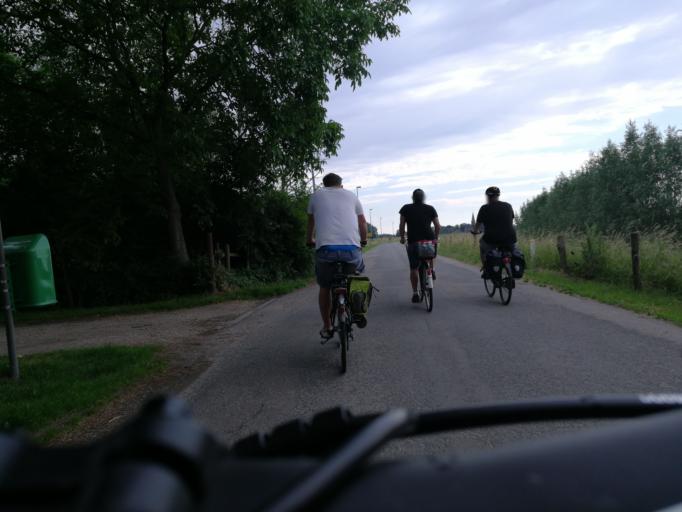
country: DE
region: North Rhine-Westphalia
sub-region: Regierungsbezirk Dusseldorf
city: Kleve
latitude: 51.8355
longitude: 6.1122
